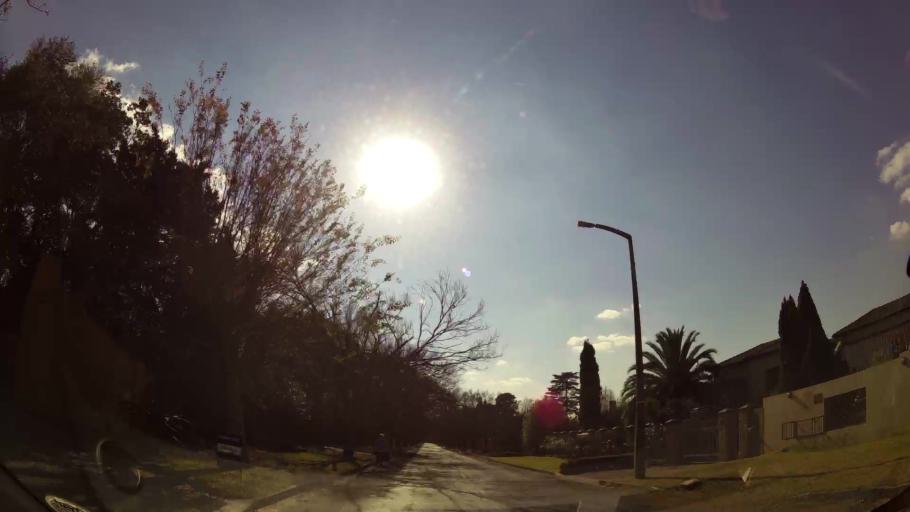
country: ZA
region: Gauteng
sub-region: Ekurhuleni Metropolitan Municipality
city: Benoni
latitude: -26.1440
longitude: 28.3461
